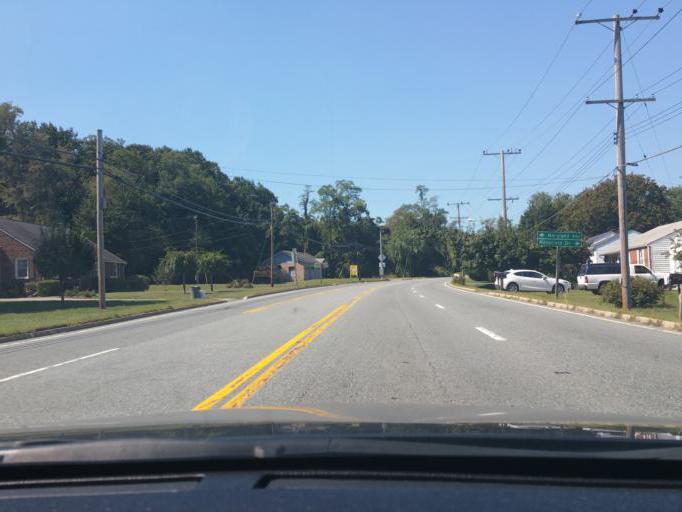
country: US
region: Maryland
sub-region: Harford County
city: Havre de Grace
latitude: 39.5618
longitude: -76.1121
